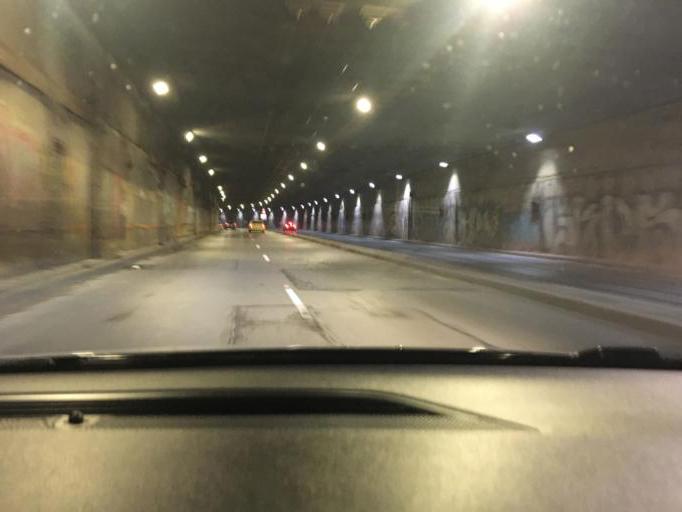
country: BG
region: Sofia-Capital
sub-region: Stolichna Obshtina
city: Sofia
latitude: 42.6873
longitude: 23.3168
